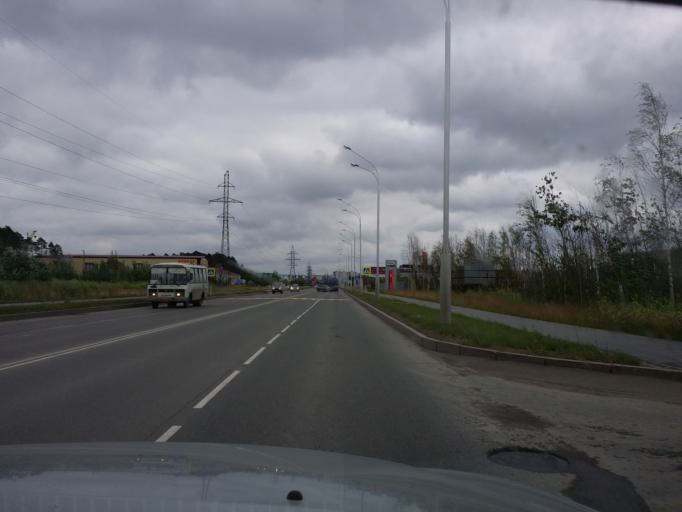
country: RU
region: Khanty-Mansiyskiy Avtonomnyy Okrug
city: Nizhnevartovsk
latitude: 60.9645
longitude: 76.5482
